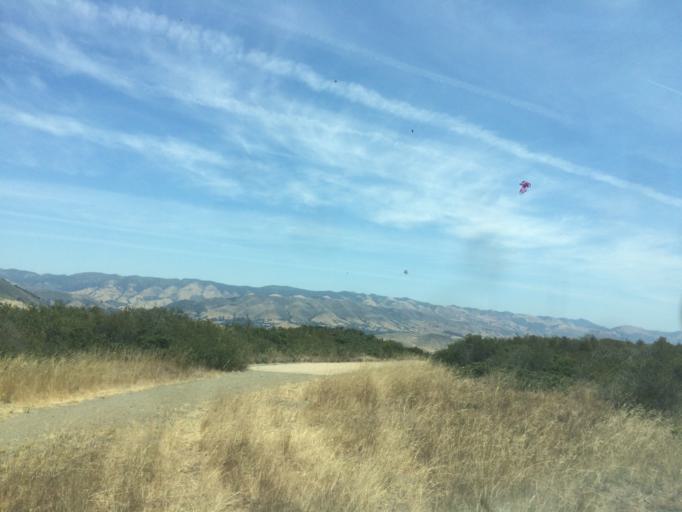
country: US
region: California
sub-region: San Luis Obispo County
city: San Luis Obispo
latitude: 35.2537
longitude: -120.7094
